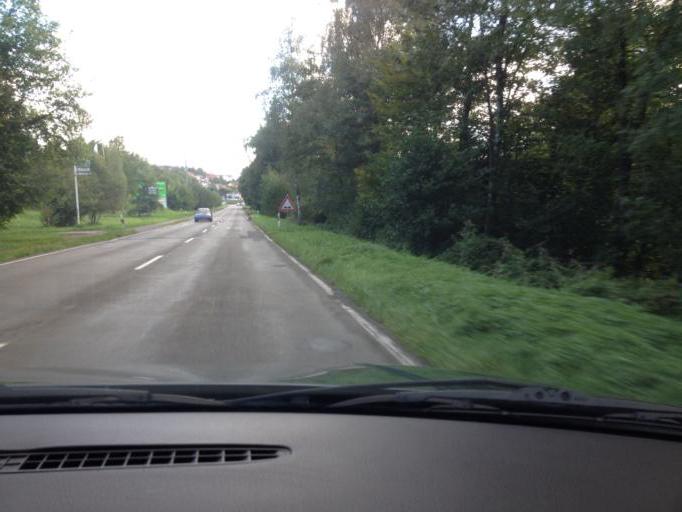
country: DE
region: Saarland
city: Marpingen
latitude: 49.4627
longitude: 7.0644
